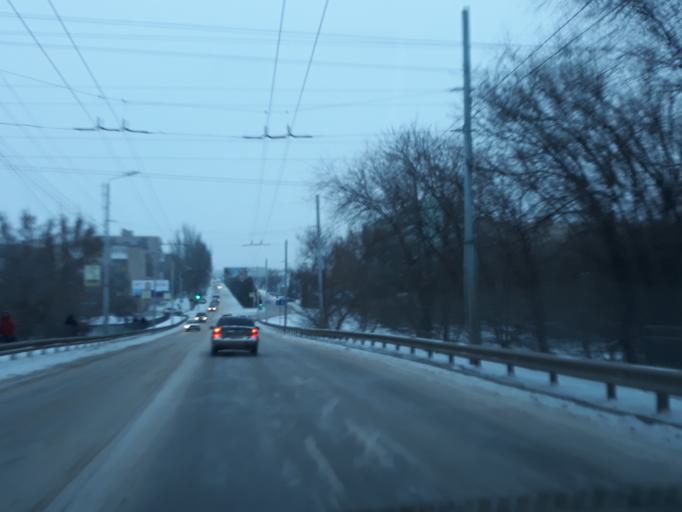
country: RU
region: Rostov
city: Taganrog
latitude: 47.2662
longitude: 38.9244
